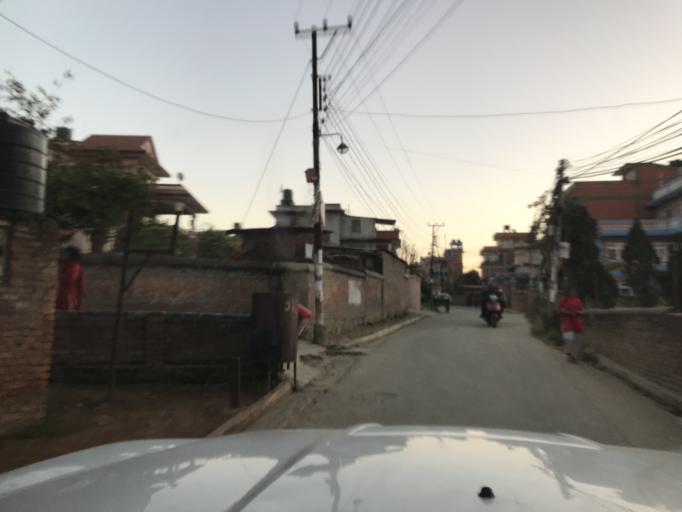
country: NP
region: Central Region
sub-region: Bagmati Zone
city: Patan
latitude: 27.6524
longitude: 85.3169
